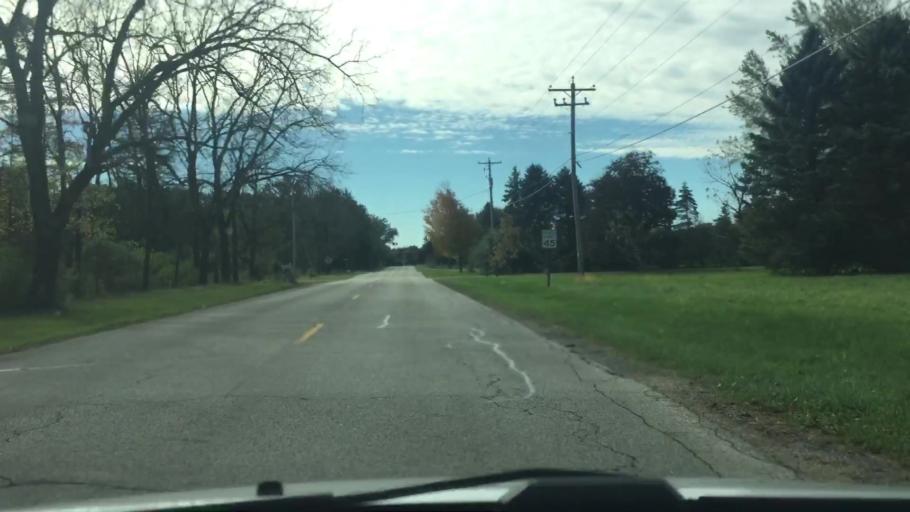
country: US
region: Wisconsin
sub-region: Waukesha County
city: Dousman
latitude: 43.0472
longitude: -88.4866
